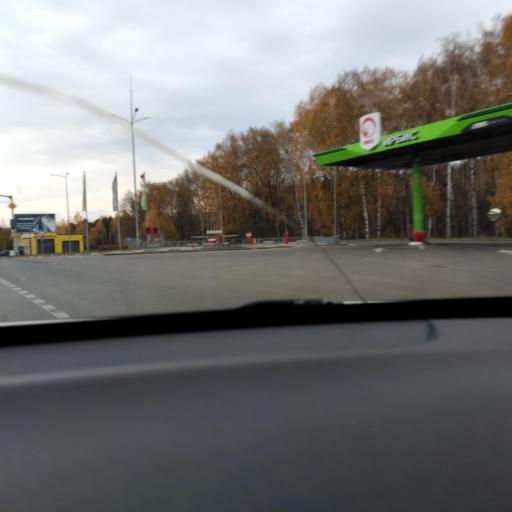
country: RU
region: Tatarstan
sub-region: Zelenodol'skiy Rayon
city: Zelenodolsk
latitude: 55.8546
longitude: 48.5745
